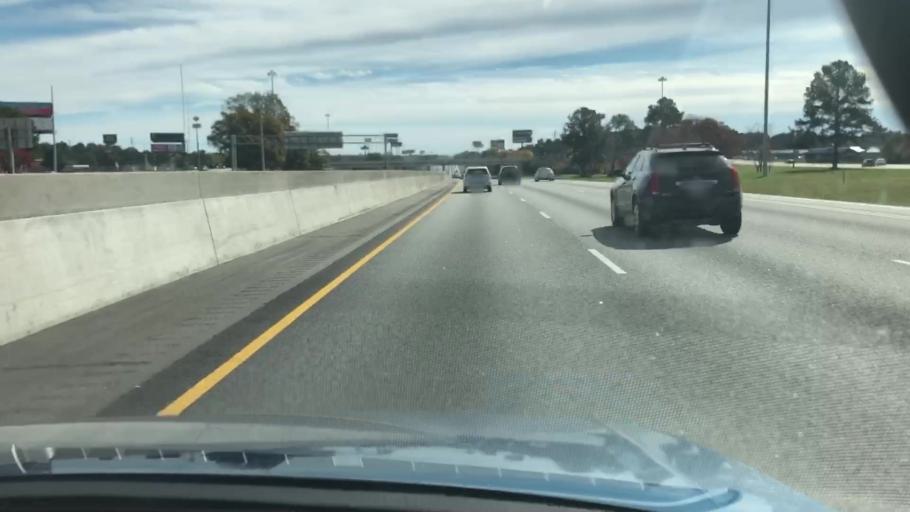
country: US
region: Georgia
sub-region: Henry County
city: McDonough
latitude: 33.4296
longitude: -84.1845
